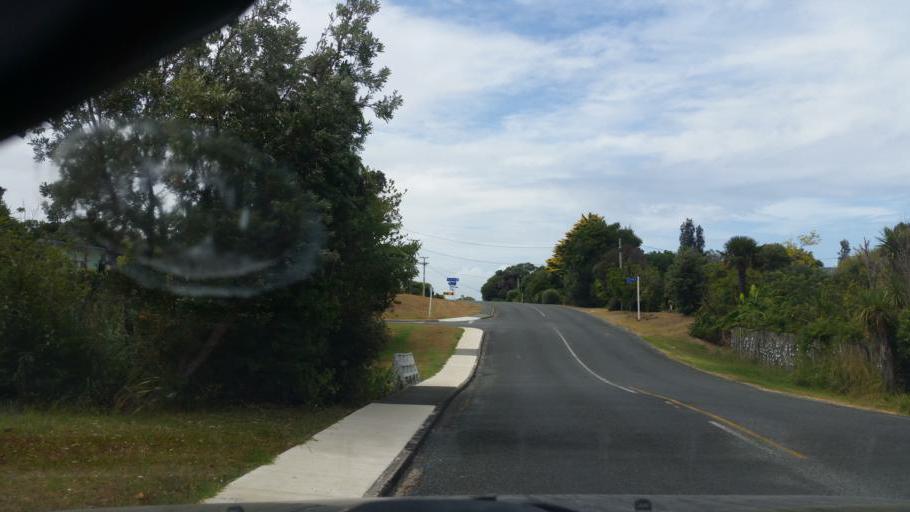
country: NZ
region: Auckland
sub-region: Auckland
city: Wellsford
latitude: -36.0866
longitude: 174.5852
